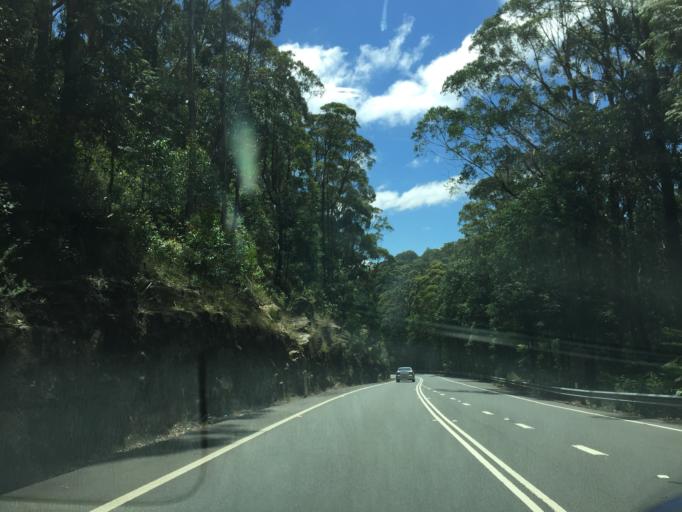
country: AU
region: New South Wales
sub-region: Blue Mountains Municipality
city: Blackheath
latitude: -33.5493
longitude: 150.4169
